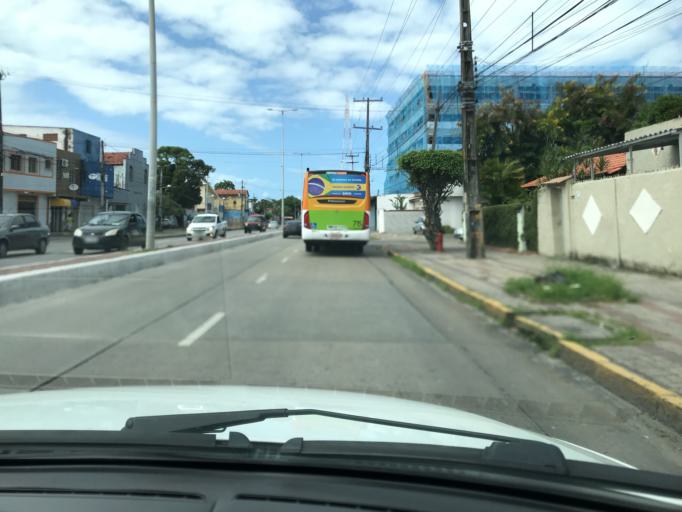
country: BR
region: Pernambuco
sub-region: Recife
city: Recife
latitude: -8.0460
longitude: -34.8790
